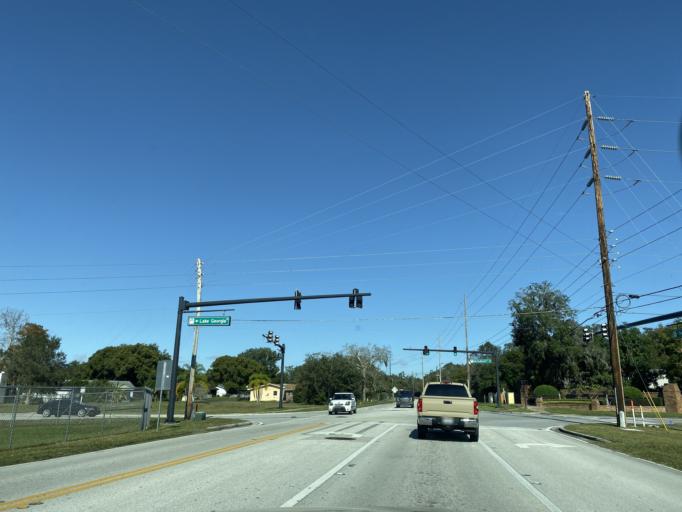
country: US
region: Florida
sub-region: Seminole County
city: Goldenrod
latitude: 28.6112
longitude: -81.2446
